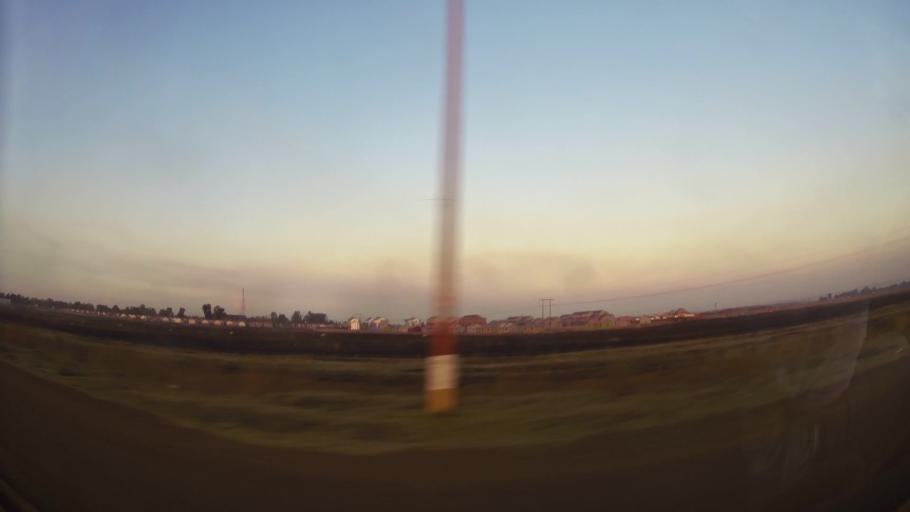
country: ZA
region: Gauteng
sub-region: Ekurhuleni Metropolitan Municipality
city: Springs
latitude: -26.3164
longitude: 28.4253
